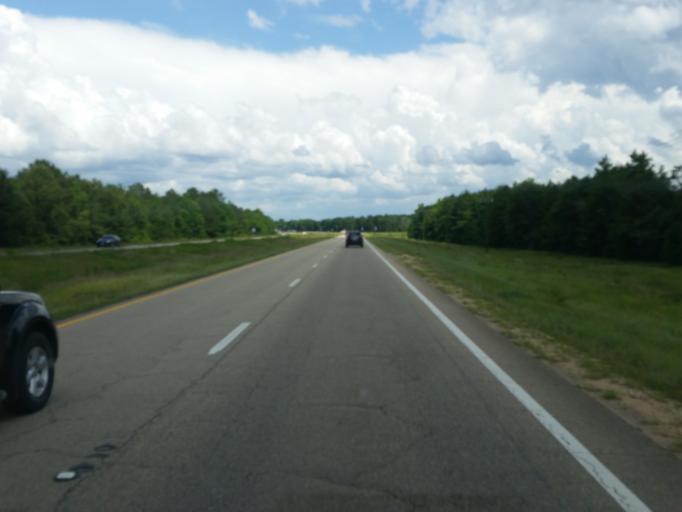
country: US
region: Mississippi
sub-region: Perry County
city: New Augusta
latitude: 31.1123
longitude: -88.8190
